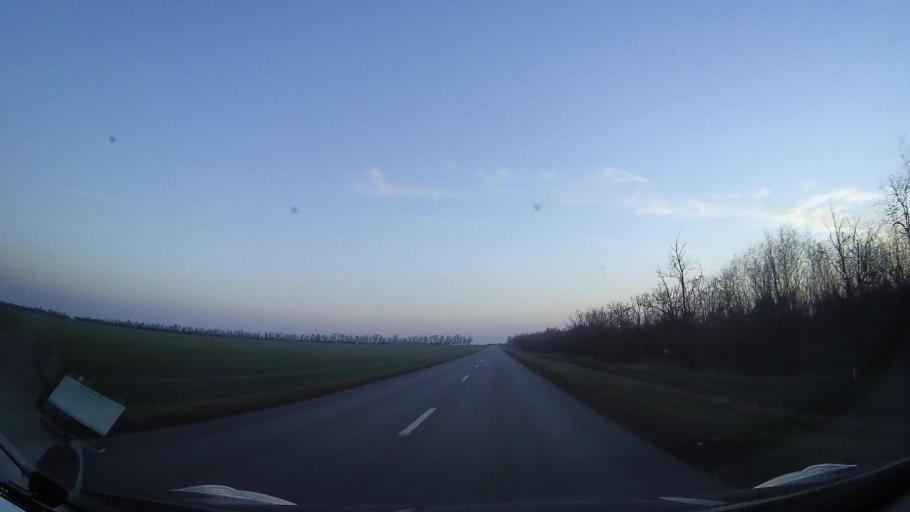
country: RU
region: Rostov
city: Zernograd
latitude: 46.9173
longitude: 40.3388
